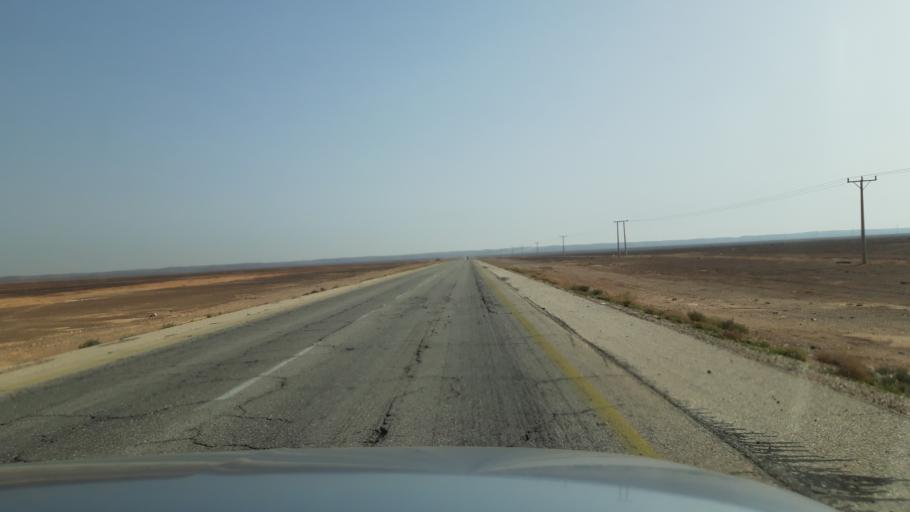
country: JO
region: Amman
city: Al Azraq ash Shamali
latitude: 31.8244
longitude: 36.6120
